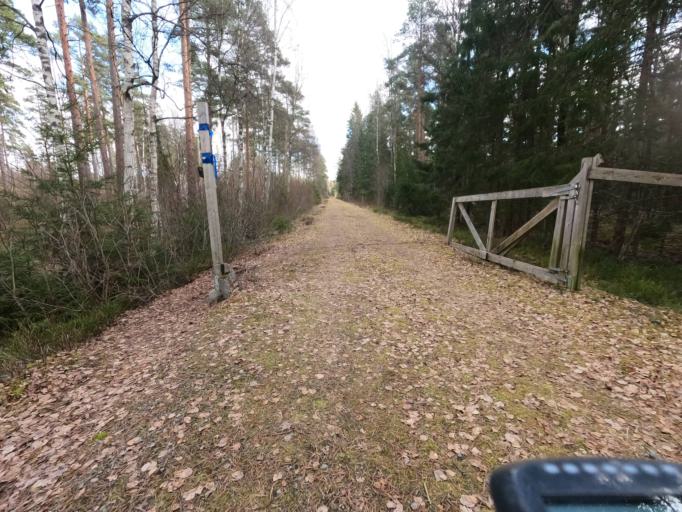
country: SE
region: Kronoberg
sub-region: Alvesta Kommun
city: Vislanda
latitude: 56.8233
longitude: 14.2956
